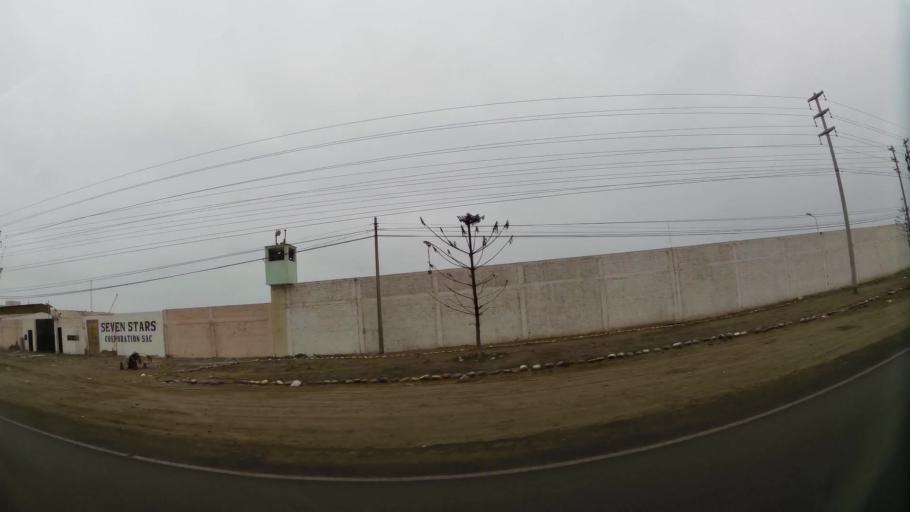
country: PE
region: Ica
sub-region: Provincia de Pisco
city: Paracas
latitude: -13.7928
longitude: -76.2396
